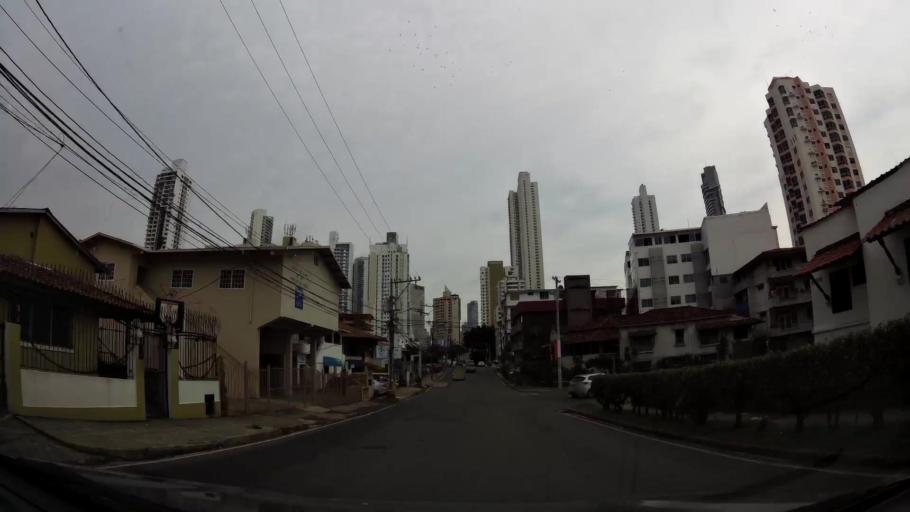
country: PA
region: Panama
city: Panama
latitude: 8.9748
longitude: -79.5332
